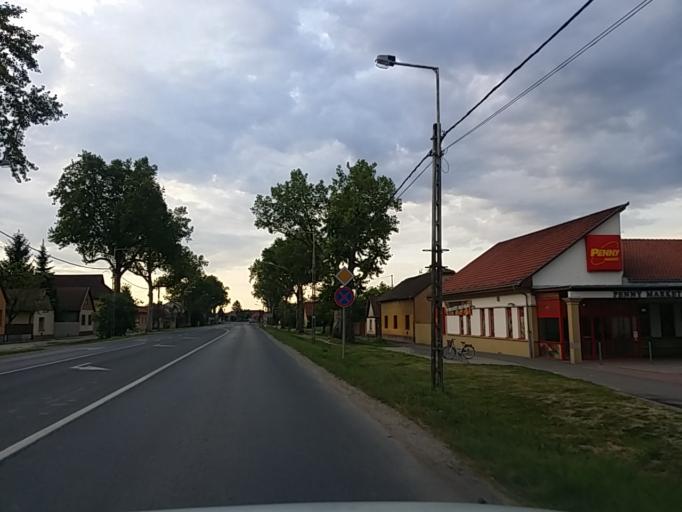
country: HU
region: Bacs-Kiskun
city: Lajosmizse
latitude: 47.0222
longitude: 19.5634
